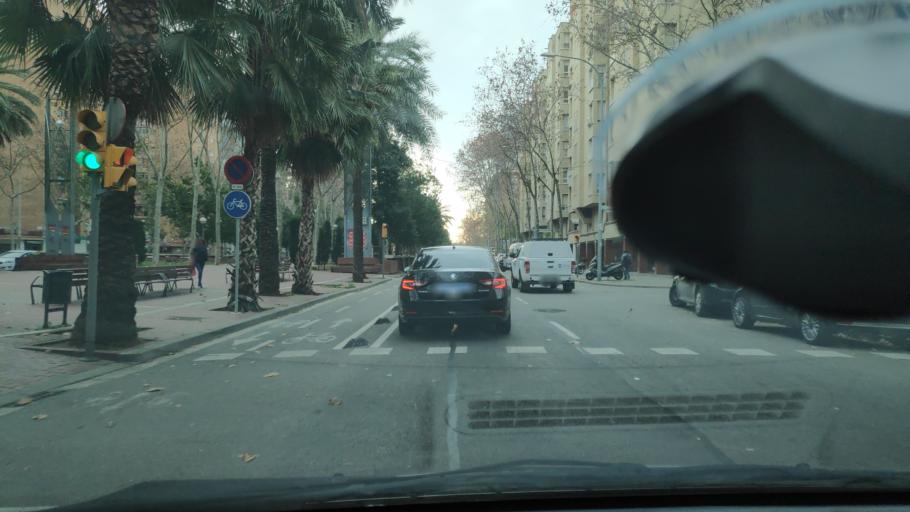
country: ES
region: Catalonia
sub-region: Provincia de Barcelona
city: Sant Marti
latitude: 41.4135
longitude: 2.2160
